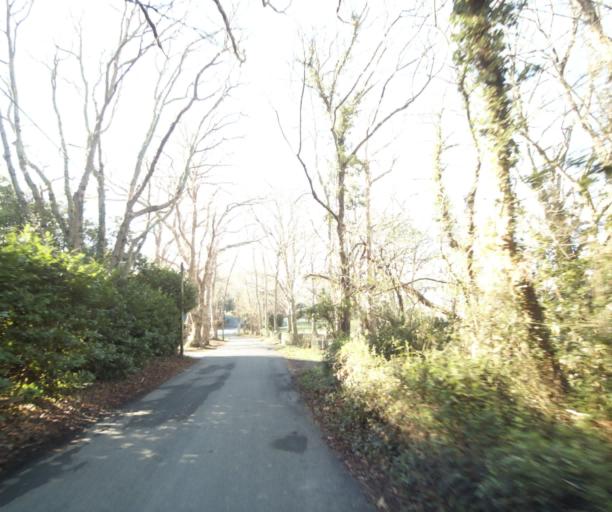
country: FR
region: Aquitaine
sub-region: Departement des Pyrenees-Atlantiques
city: Ciboure
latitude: 43.3640
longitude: -1.6608
